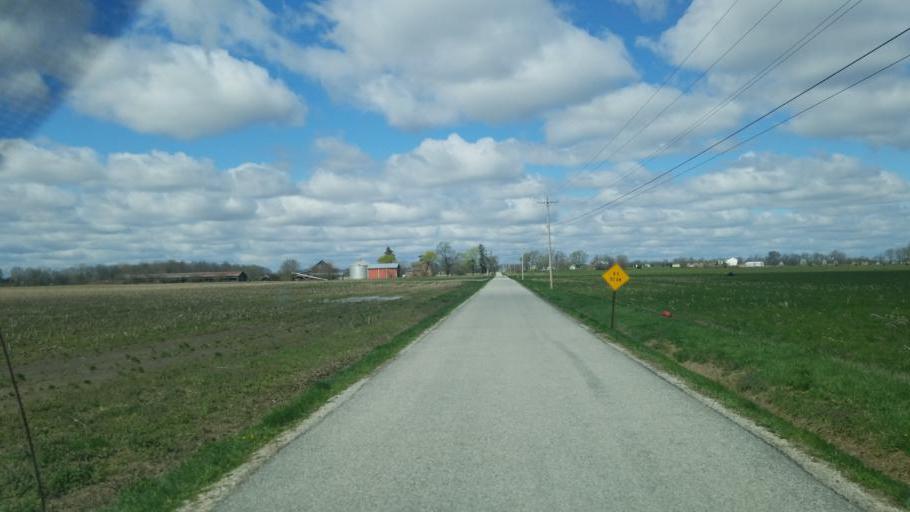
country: US
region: Ohio
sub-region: Delaware County
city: Delaware
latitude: 40.3554
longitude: -83.1221
